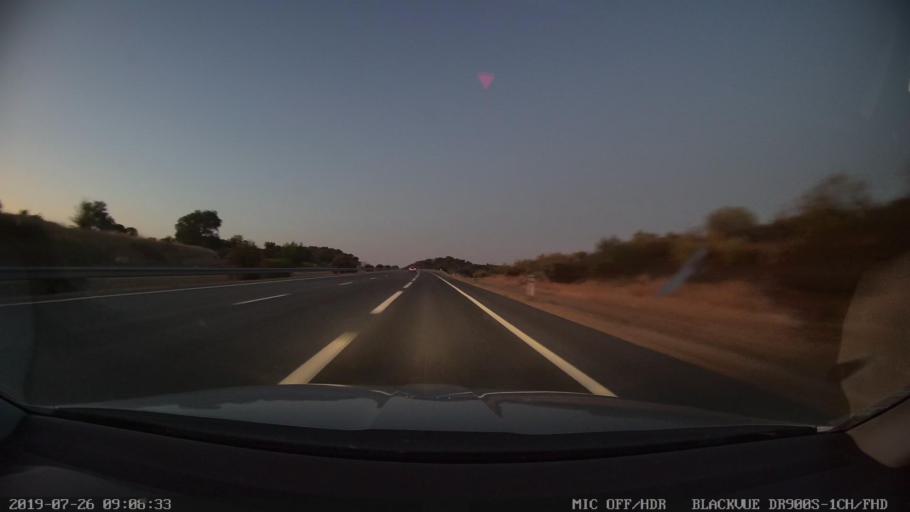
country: PT
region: Evora
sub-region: Estremoz
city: Estremoz
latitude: 38.7557
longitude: -7.7144
